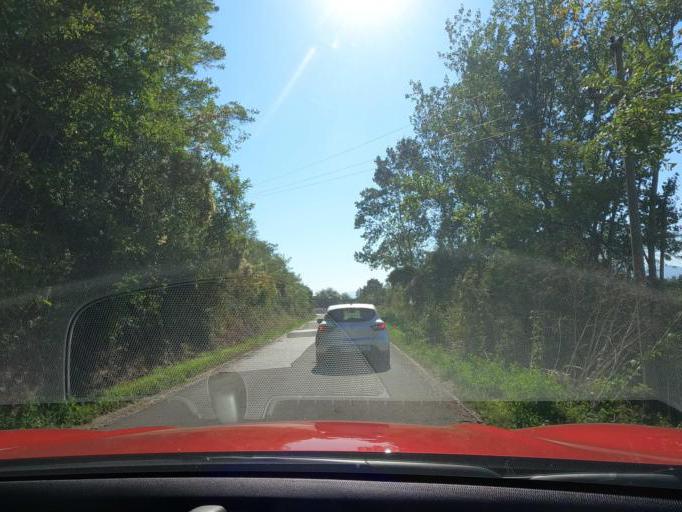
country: RS
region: Central Serbia
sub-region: Raski Okrug
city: Kraljevo
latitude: 43.7336
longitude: 20.7426
